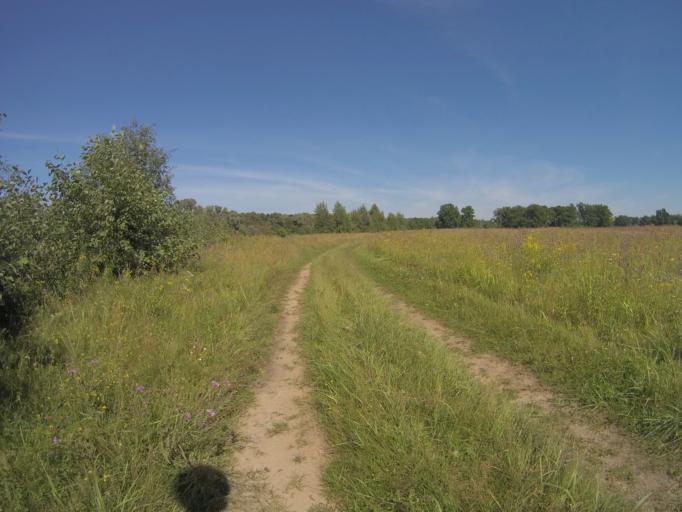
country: RU
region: Vladimir
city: Raduzhnyy
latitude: 56.0370
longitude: 40.2522
